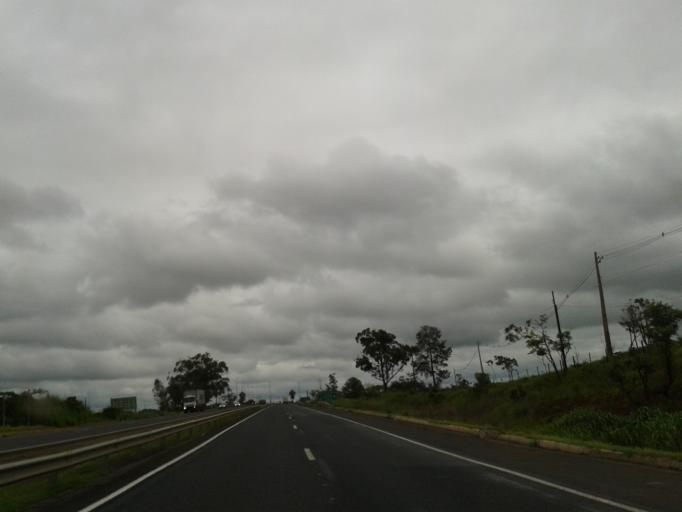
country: BR
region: Minas Gerais
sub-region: Uberlandia
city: Uberlandia
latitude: -18.9438
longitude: -48.2185
